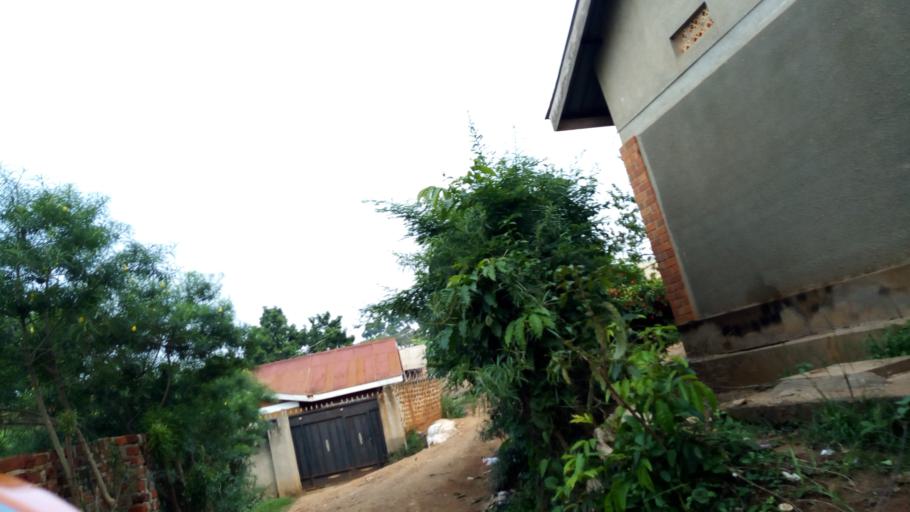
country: UG
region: Central Region
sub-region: Wakiso District
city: Kireka
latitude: 0.3138
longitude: 32.6481
